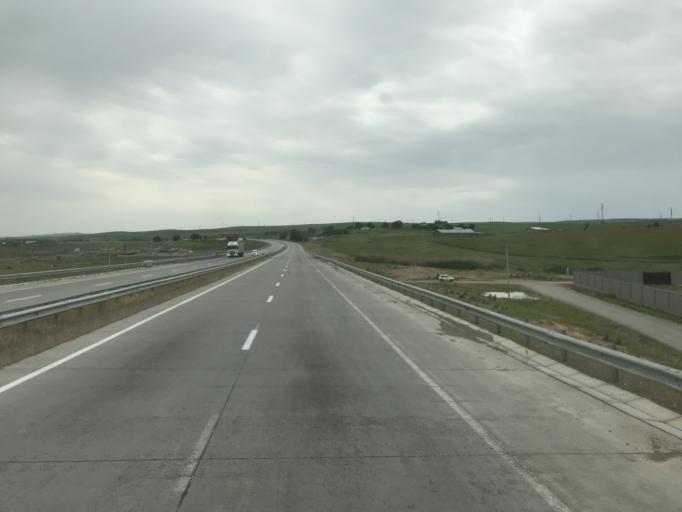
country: KZ
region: Ongtustik Qazaqstan
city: Qazyqurt
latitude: 41.8699
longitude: 69.4206
